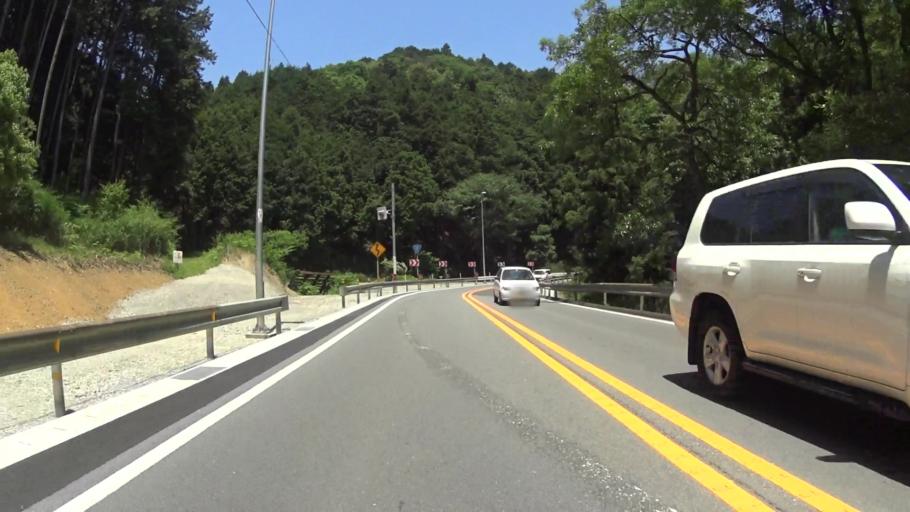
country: JP
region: Kyoto
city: Muko
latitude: 34.9875
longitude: 135.6528
